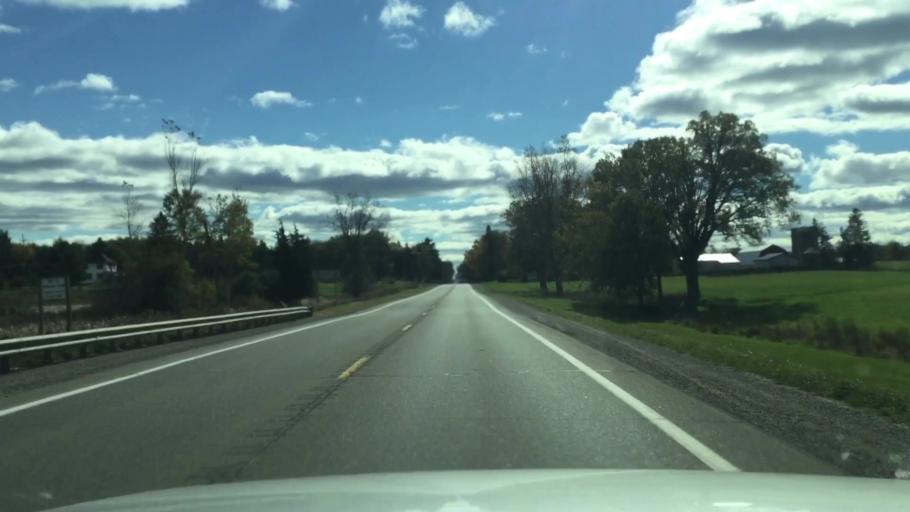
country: US
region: Michigan
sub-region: Lapeer County
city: Barnes Lake-Millers Lake
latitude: 43.1457
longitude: -83.3111
